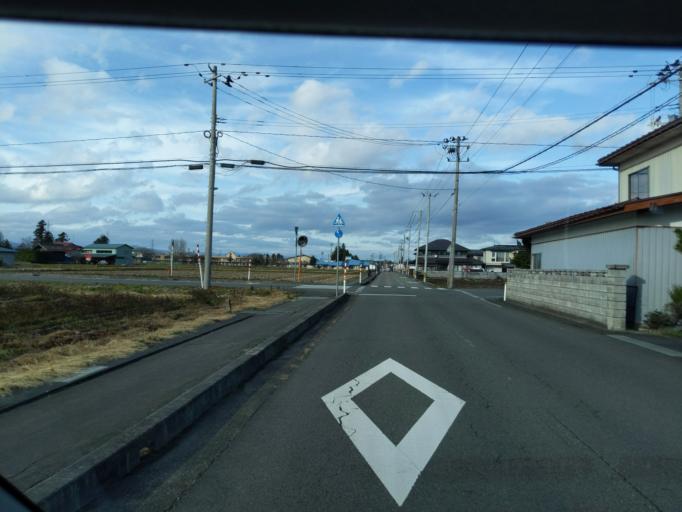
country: JP
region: Iwate
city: Mizusawa
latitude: 39.1353
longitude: 141.0904
